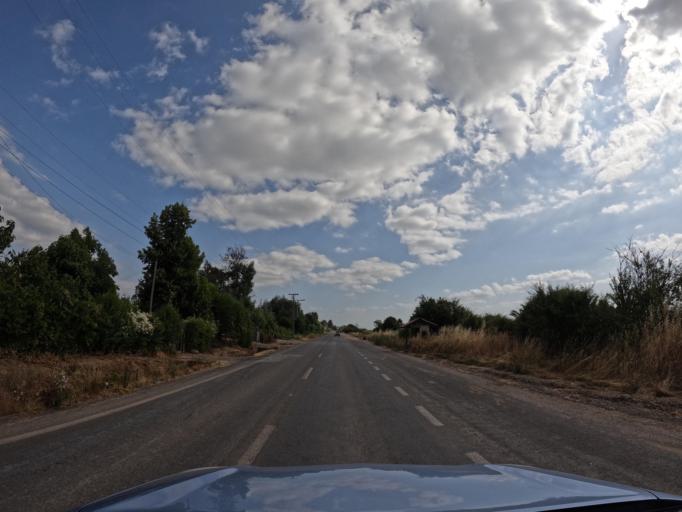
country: CL
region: Maule
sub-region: Provincia de Curico
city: Molina
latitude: -35.1870
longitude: -71.2957
